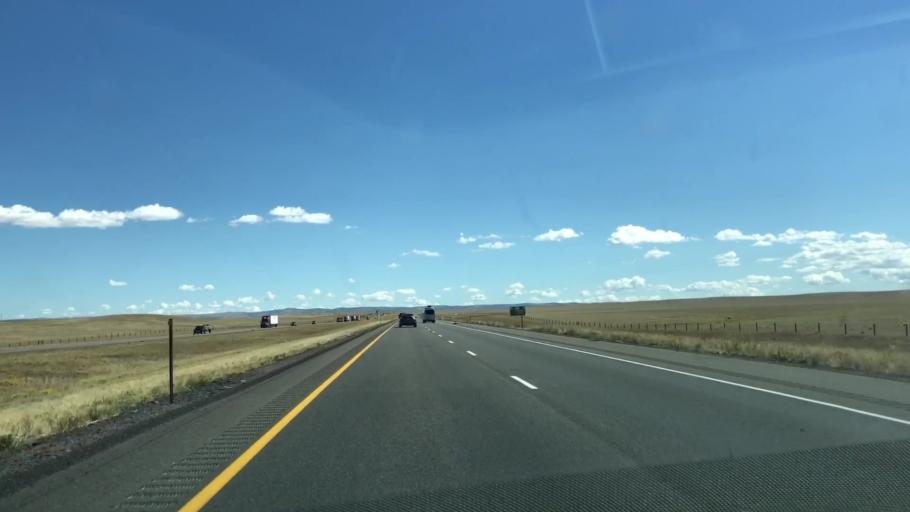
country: US
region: Wyoming
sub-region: Albany County
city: Laramie
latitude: 41.3603
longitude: -105.7657
